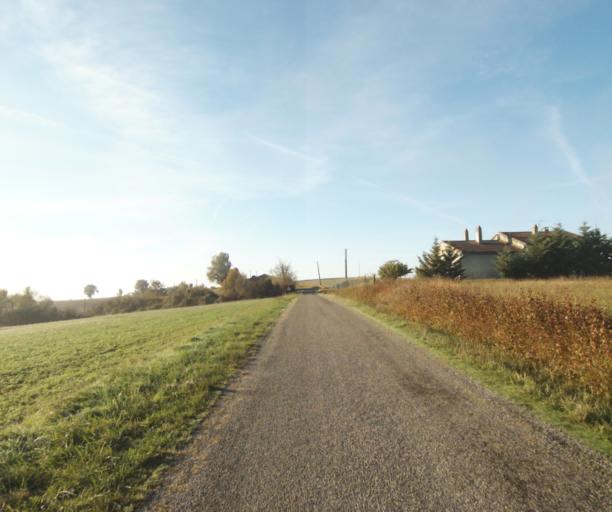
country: FR
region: Midi-Pyrenees
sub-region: Departement du Tarn-et-Garonne
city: Nohic
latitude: 43.9016
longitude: 1.4776
